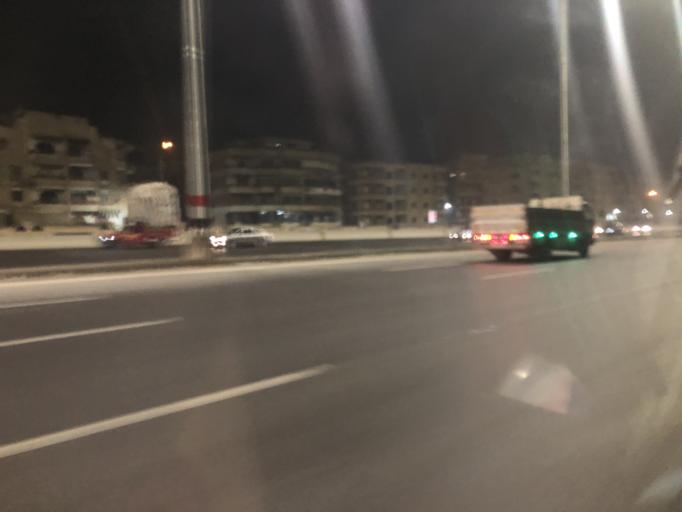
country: EG
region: Al Jizah
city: Al Jizah
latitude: 29.9746
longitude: 31.1107
